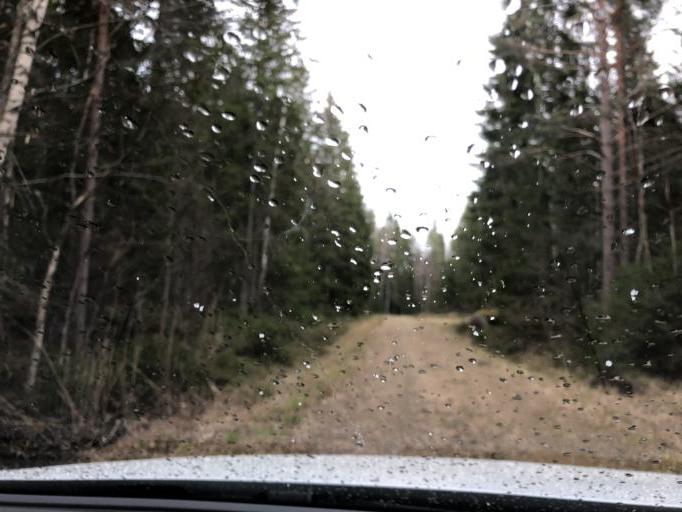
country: SE
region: Gaevleborg
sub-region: Gavle Kommun
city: Hedesunda
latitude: 60.3408
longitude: 17.0825
